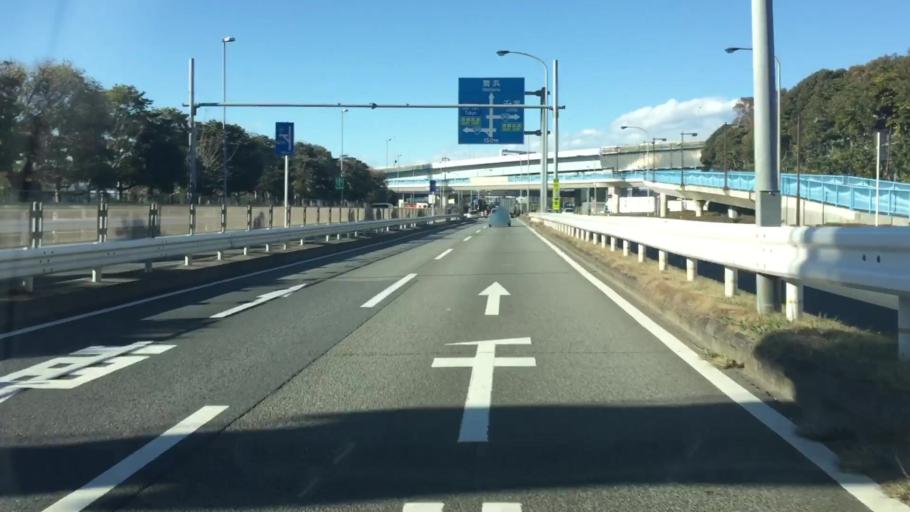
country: JP
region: Tokyo
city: Urayasu
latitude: 35.6359
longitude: 139.8862
